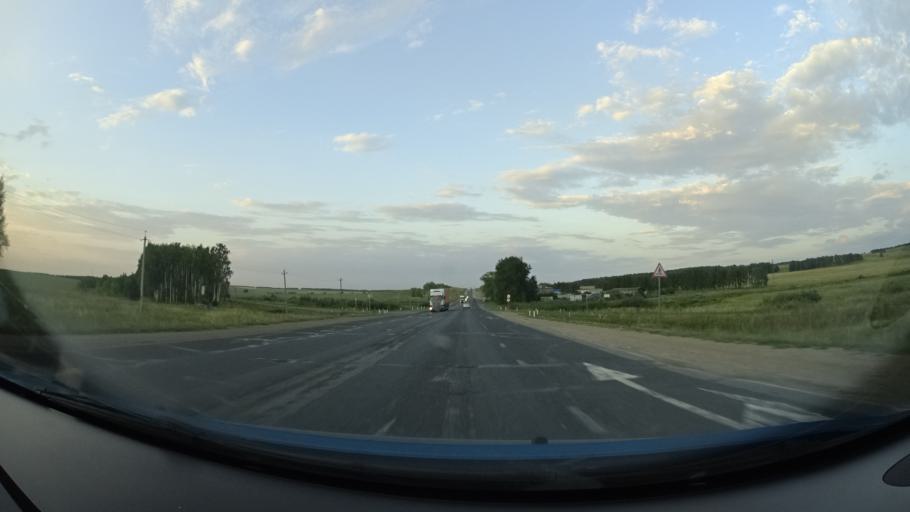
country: RU
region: Orenburg
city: Severnoye
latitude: 54.2125
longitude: 52.7097
